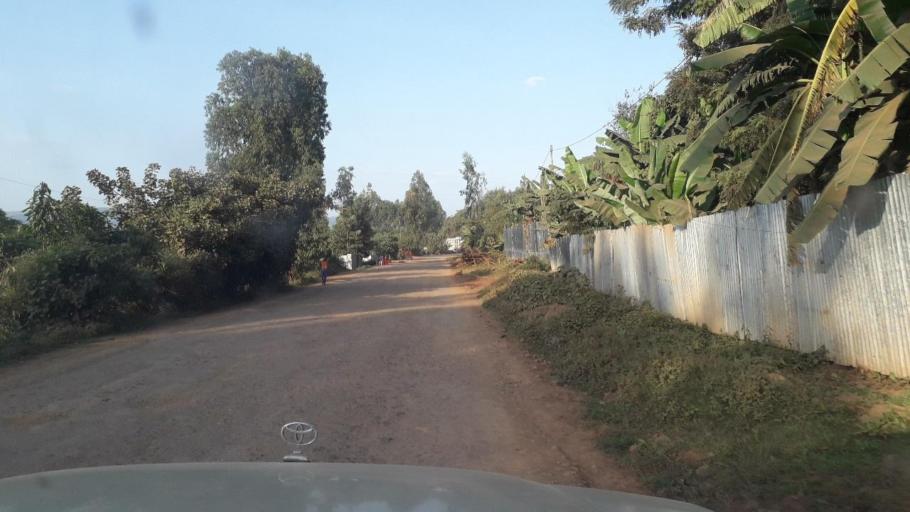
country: ET
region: Oromiya
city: Jima
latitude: 7.6329
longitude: 36.8324
